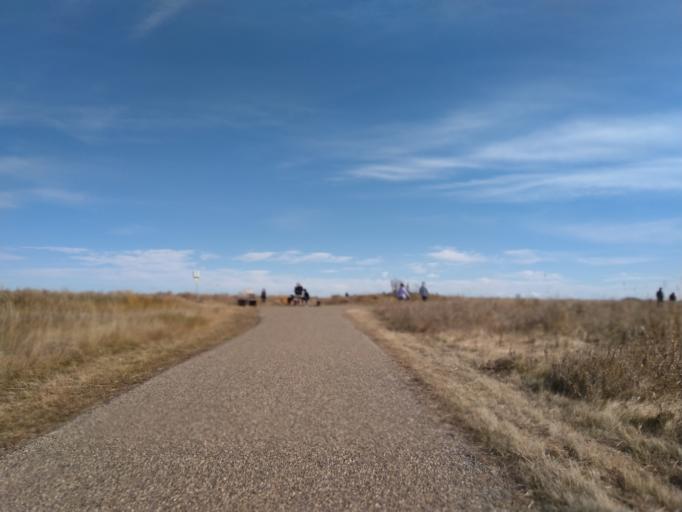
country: CA
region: Alberta
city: Calgary
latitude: 51.1106
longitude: -114.1185
